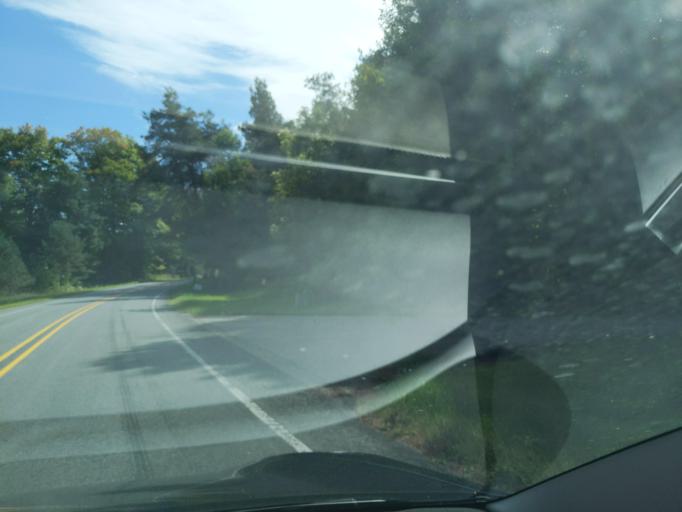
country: US
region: Michigan
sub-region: Antrim County
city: Bellaire
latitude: 44.9897
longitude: -85.2847
